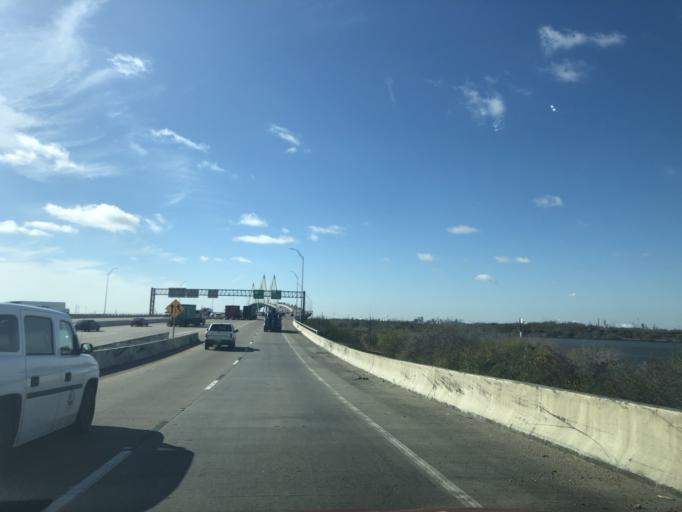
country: US
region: Texas
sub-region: Harris County
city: Baytown
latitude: 29.7135
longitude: -95.0022
